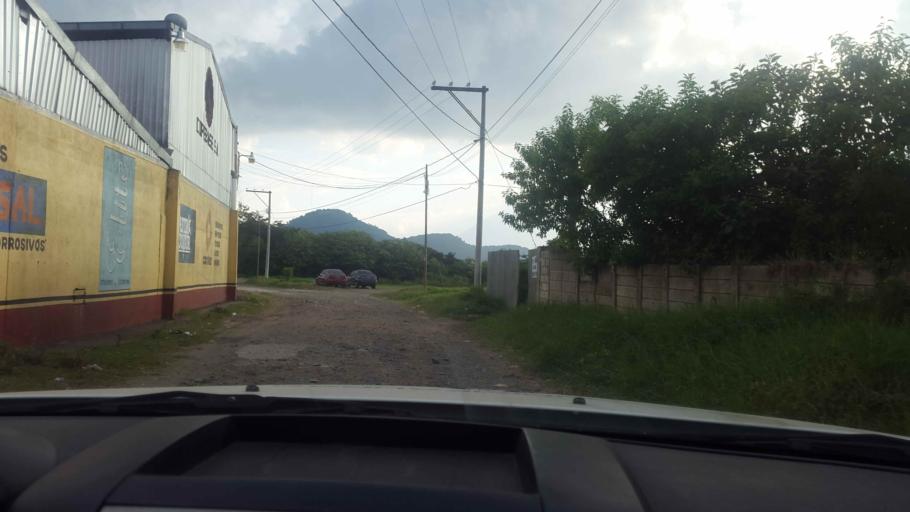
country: GT
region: Guatemala
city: Petapa
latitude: 14.5113
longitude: -90.5446
